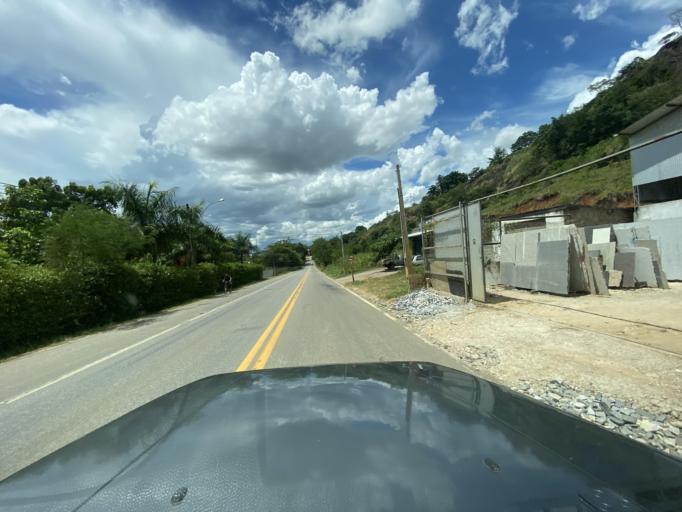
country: BR
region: Espirito Santo
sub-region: Jeronimo Monteiro
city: Jeronimo Monteiro
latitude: -20.7933
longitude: -41.3969
